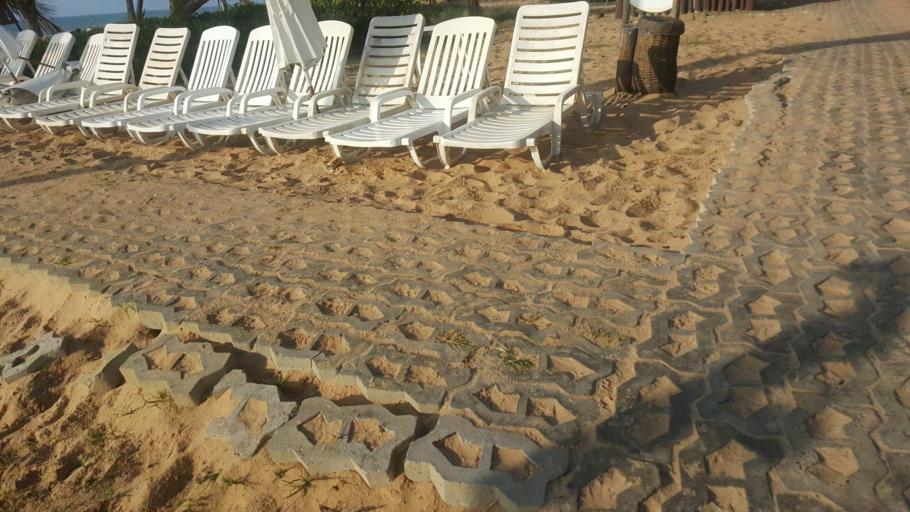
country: BR
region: Bahia
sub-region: Mata De Sao Joao
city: Mata de Sao Joao
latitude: -12.4380
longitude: -37.9157
